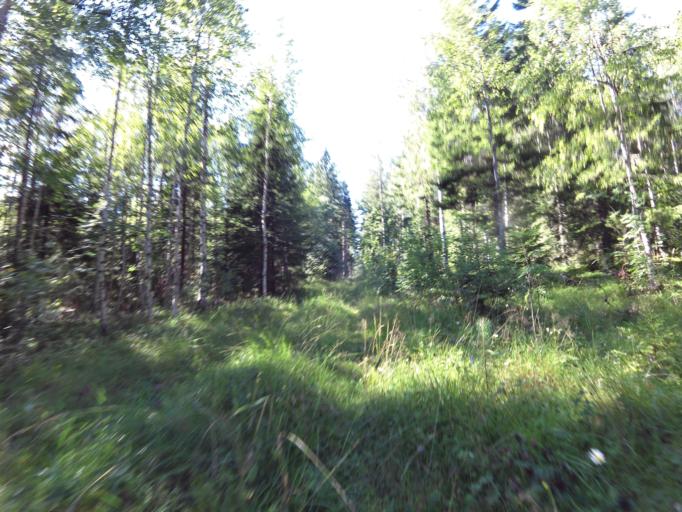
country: SE
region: Gaevleborg
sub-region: Hofors Kommun
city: Hofors
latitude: 60.5700
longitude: 16.4658
